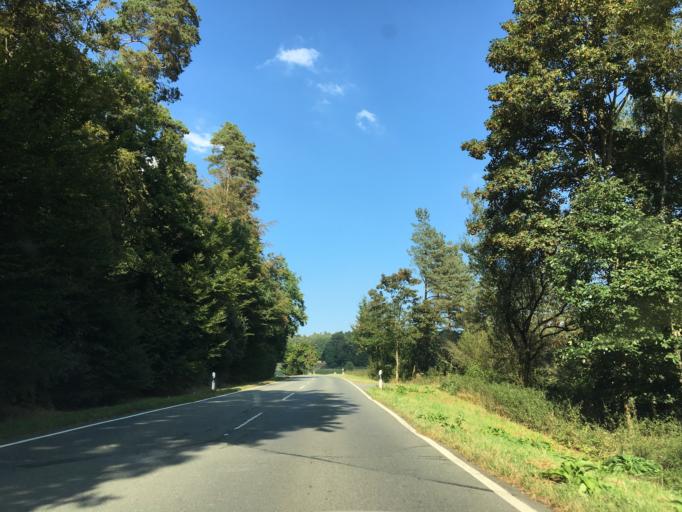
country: DE
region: Hesse
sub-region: Regierungsbezirk Giessen
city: Munchhausen
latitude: 50.9932
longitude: 8.7449
